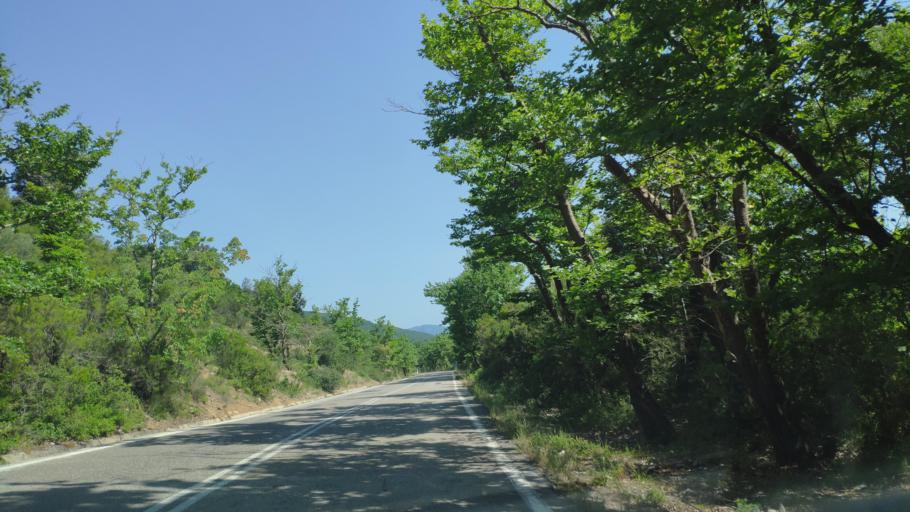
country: GR
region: West Greece
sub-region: Nomos Aitolias kai Akarnanias
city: Lepenou
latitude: 38.7899
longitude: 21.3333
